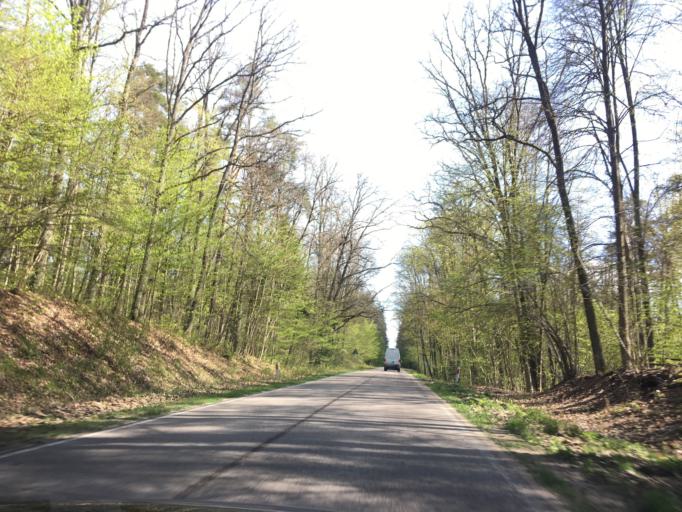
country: PL
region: Warmian-Masurian Voivodeship
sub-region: Powiat piski
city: Ruciane-Nida
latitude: 53.6654
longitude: 21.5694
